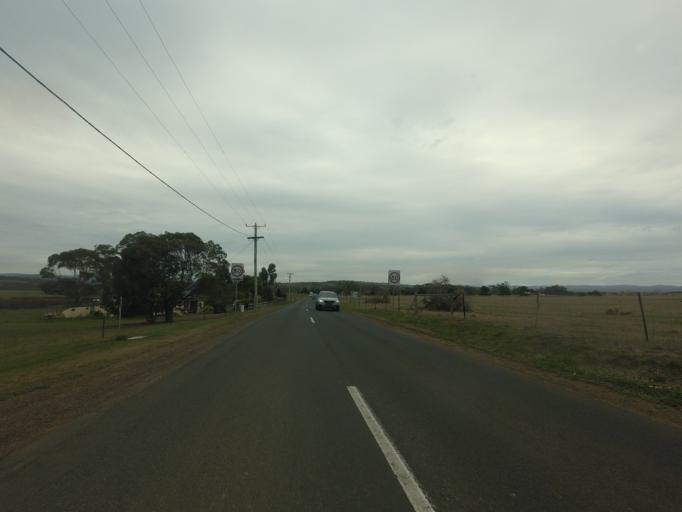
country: AU
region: Tasmania
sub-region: Break O'Day
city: St Helens
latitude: -42.1200
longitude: 148.0670
